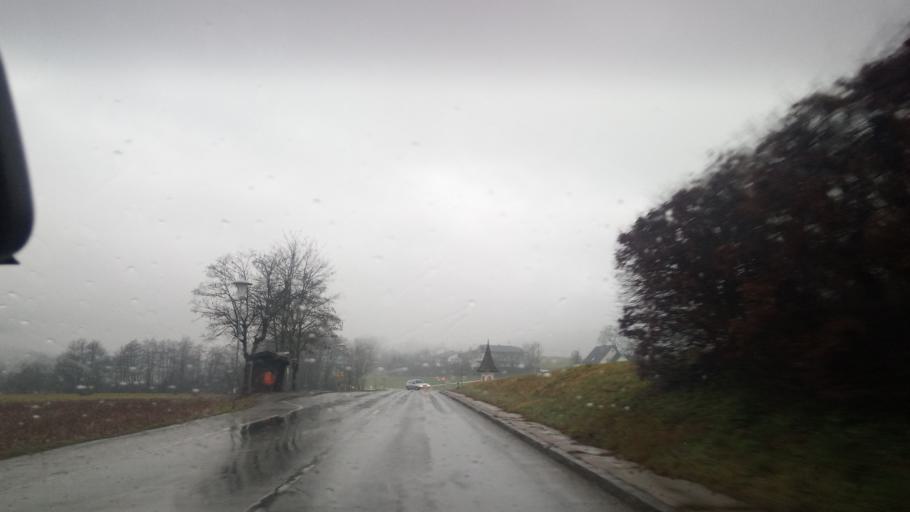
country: AT
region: Carinthia
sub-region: Politischer Bezirk Klagenfurt Land
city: Kottmannsdorf
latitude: 46.5888
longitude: 14.2326
